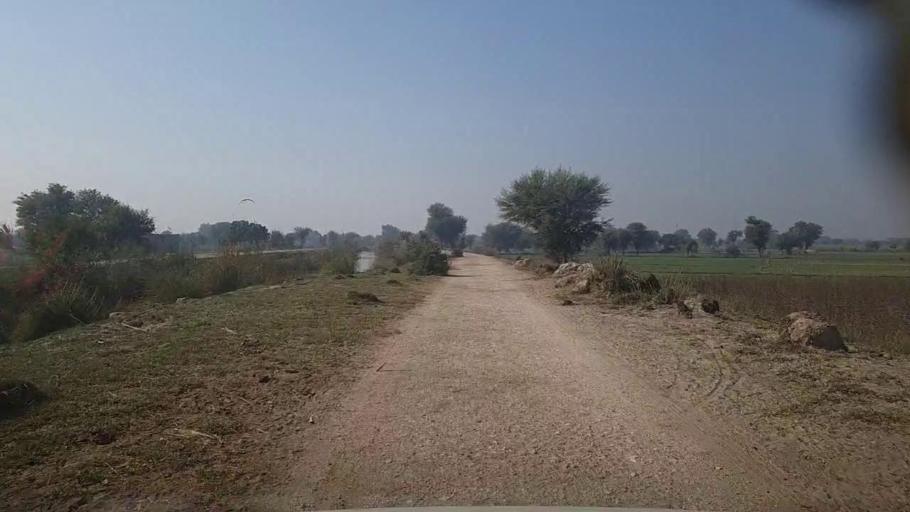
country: PK
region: Sindh
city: Kandiari
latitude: 27.0037
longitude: 68.4927
